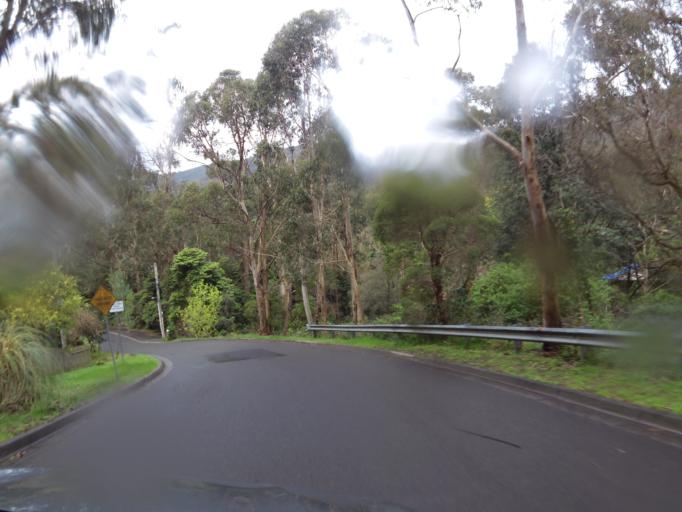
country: AU
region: Victoria
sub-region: Knox
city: The Basin
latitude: -37.8635
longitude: 145.3200
